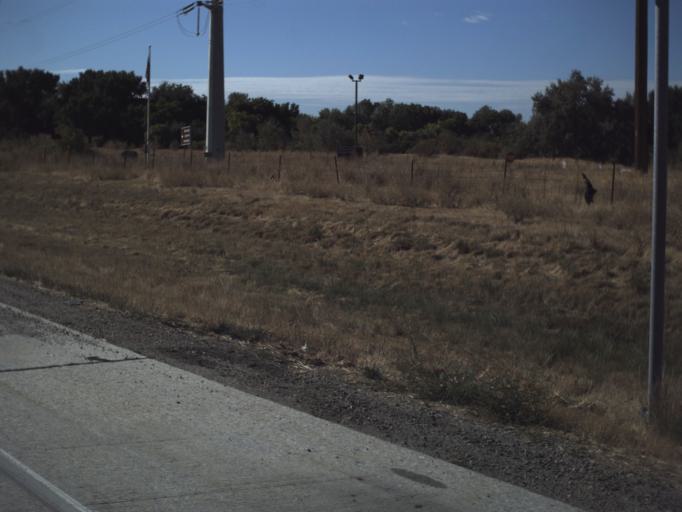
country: US
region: Utah
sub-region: Box Elder County
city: Willard
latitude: 41.4224
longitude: -112.0539
